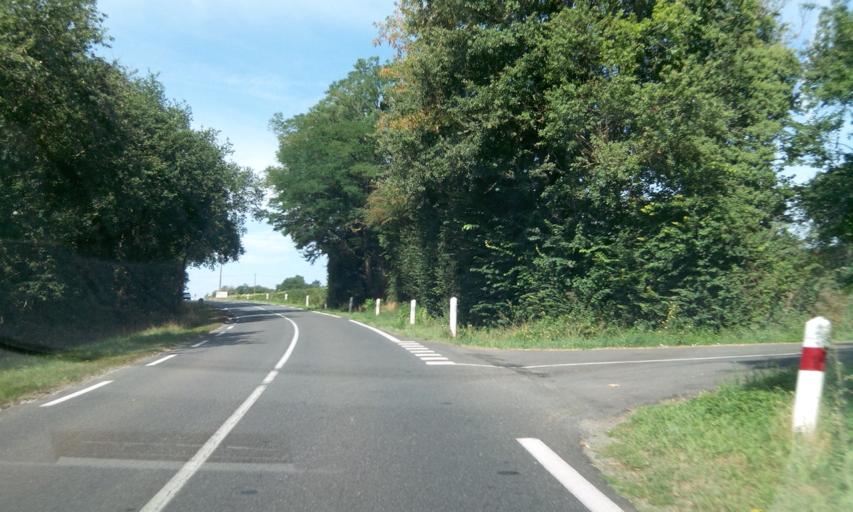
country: FR
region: Poitou-Charentes
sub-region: Departement de la Vienne
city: Savigne
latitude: 46.1595
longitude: 0.3478
